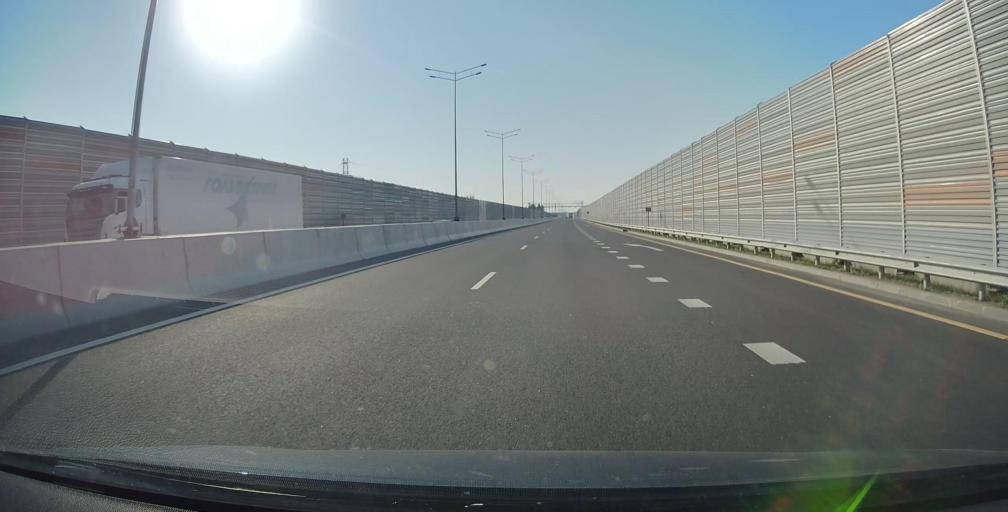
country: RU
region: Moskovskaya
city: Zelenogradskiy
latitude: 56.1280
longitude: 37.8940
